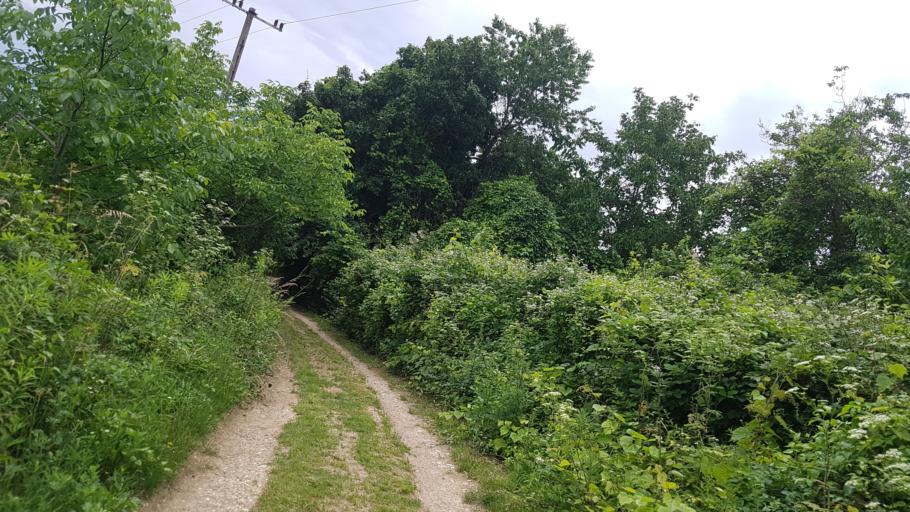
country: HU
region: Pest
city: Urom
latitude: 47.6157
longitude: 19.0171
